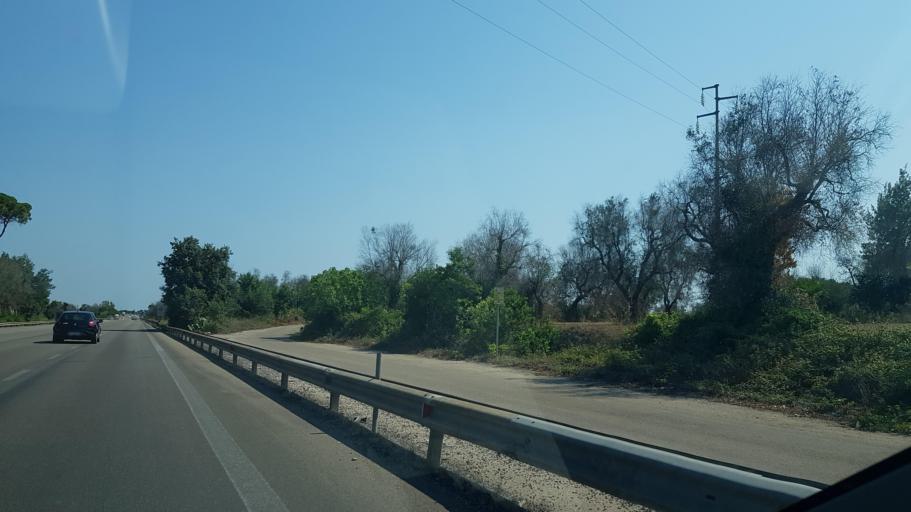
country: IT
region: Apulia
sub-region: Provincia di Lecce
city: Scorrano
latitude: 40.1019
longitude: 18.3159
